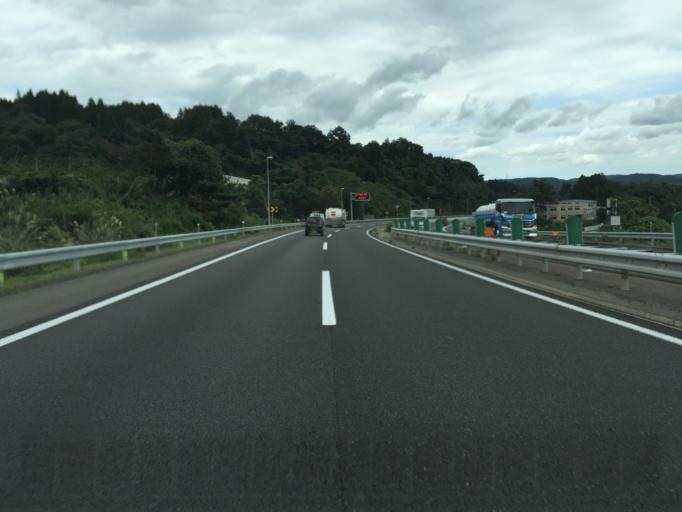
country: JP
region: Miyagi
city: Okawara
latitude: 38.1186
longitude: 140.7062
